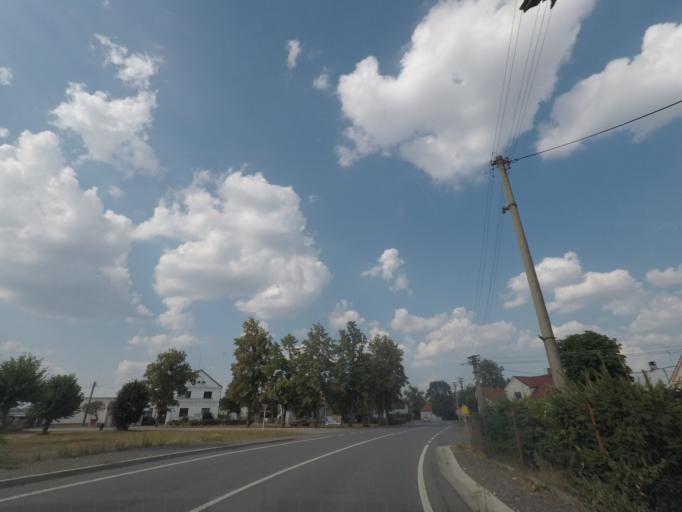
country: CZ
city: Albrechtice nad Orlici
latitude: 50.1191
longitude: 16.0688
